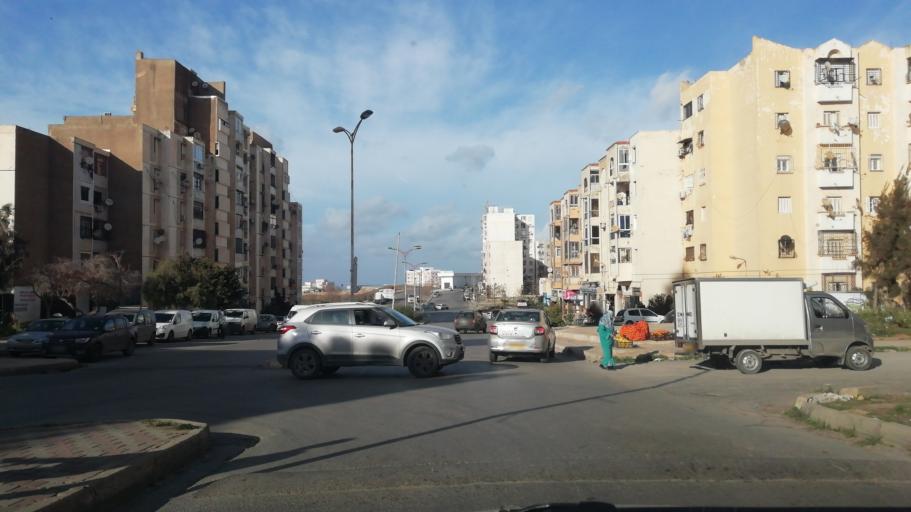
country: DZ
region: Oran
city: Bir el Djir
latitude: 35.7186
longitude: -0.5961
